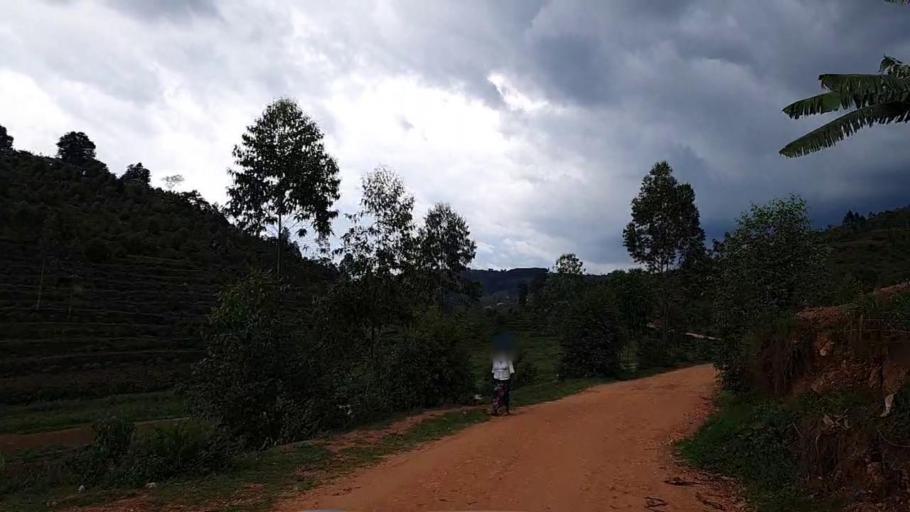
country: RW
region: Southern Province
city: Nyanza
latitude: -2.3922
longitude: 29.6899
